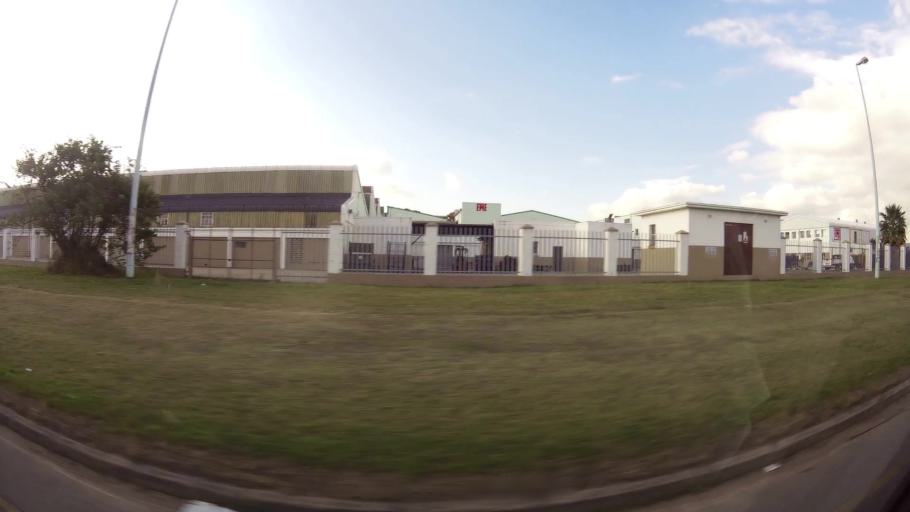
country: ZA
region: Eastern Cape
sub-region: Nelson Mandela Bay Metropolitan Municipality
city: Uitenhage
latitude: -33.7846
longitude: 25.4214
